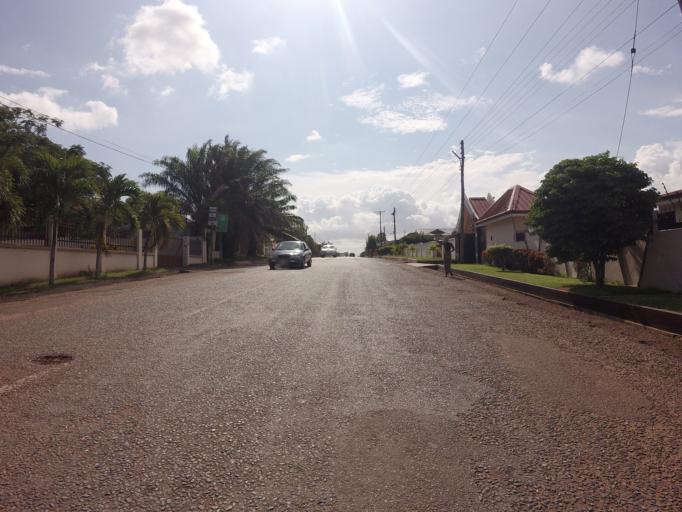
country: GH
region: Greater Accra
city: Medina Estates
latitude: 5.6688
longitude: -0.1833
